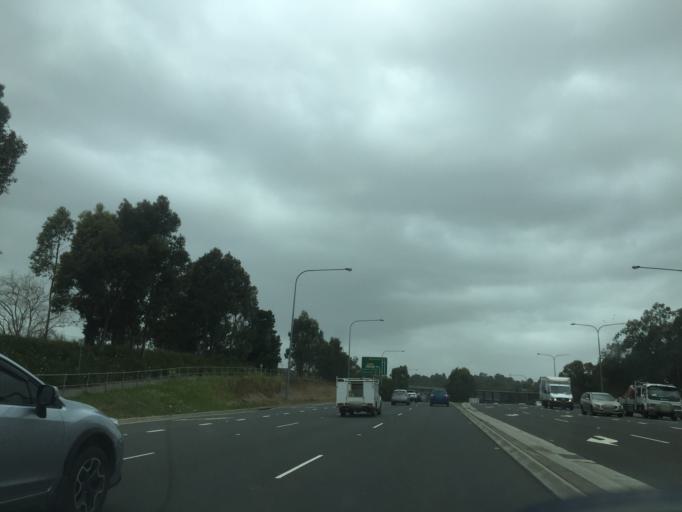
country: AU
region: New South Wales
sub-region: Blacktown
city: Blacktown
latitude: -33.7483
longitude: 150.9504
